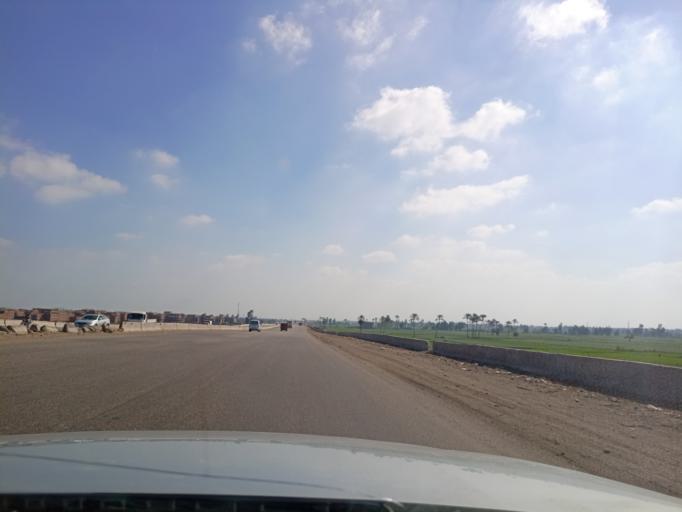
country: EG
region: Eastern Province
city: Mashtul as Suq
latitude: 30.4611
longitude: 31.3827
